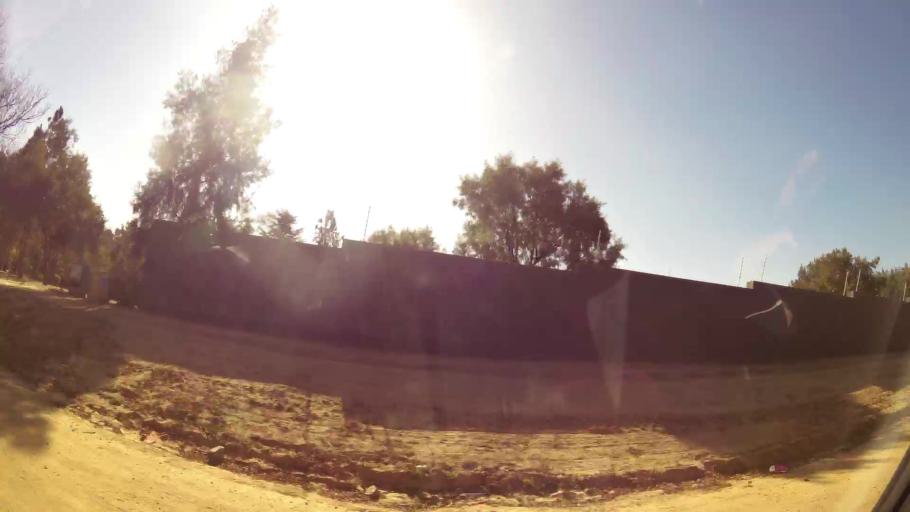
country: ZA
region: Gauteng
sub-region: City of Johannesburg Metropolitan Municipality
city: Diepsloot
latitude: -26.0114
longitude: 27.9533
